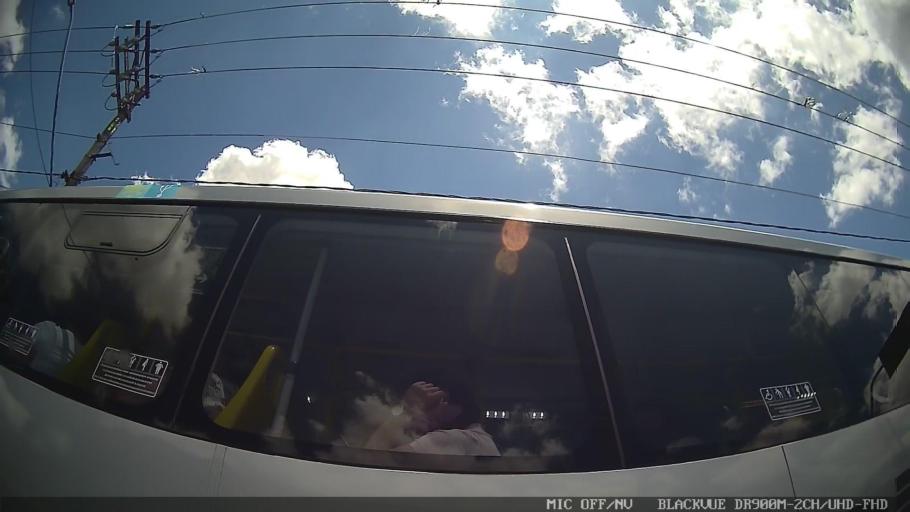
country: BR
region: Sao Paulo
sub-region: Diadema
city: Diadema
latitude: -23.6544
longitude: -46.6486
